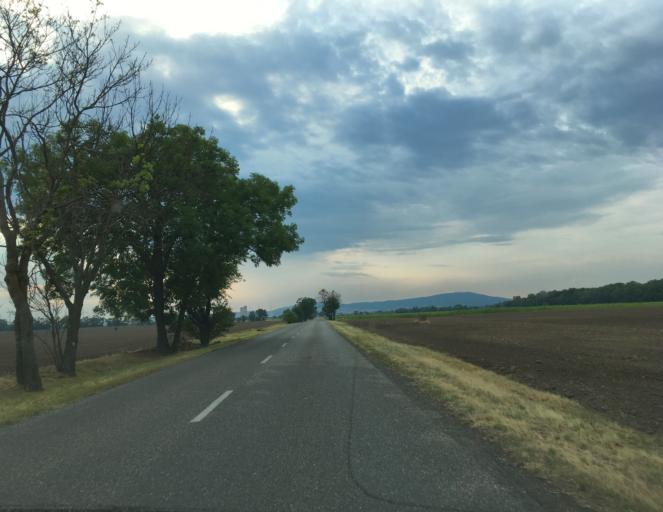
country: AT
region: Burgenland
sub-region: Politischer Bezirk Neusiedl am See
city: Kittsee
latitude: 48.0735
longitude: 17.0914
